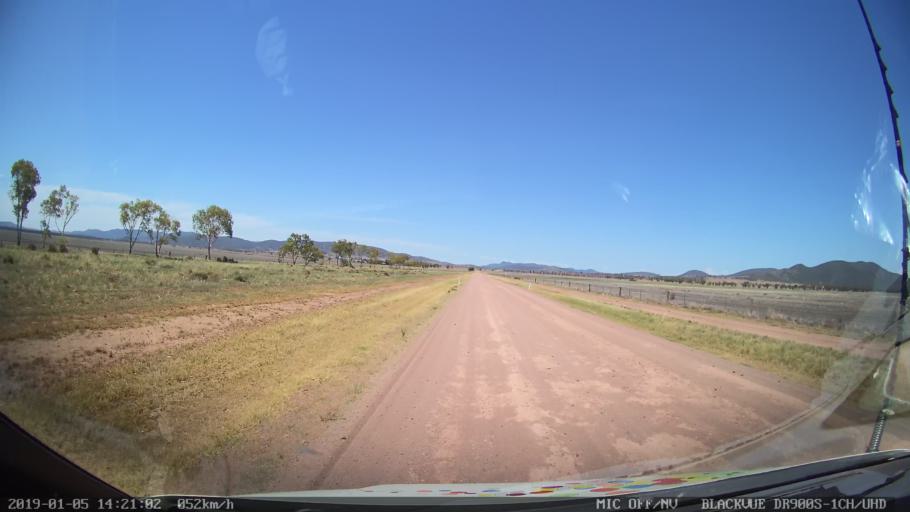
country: AU
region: New South Wales
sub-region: Liverpool Plains
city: Quirindi
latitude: -31.2474
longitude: 150.5098
